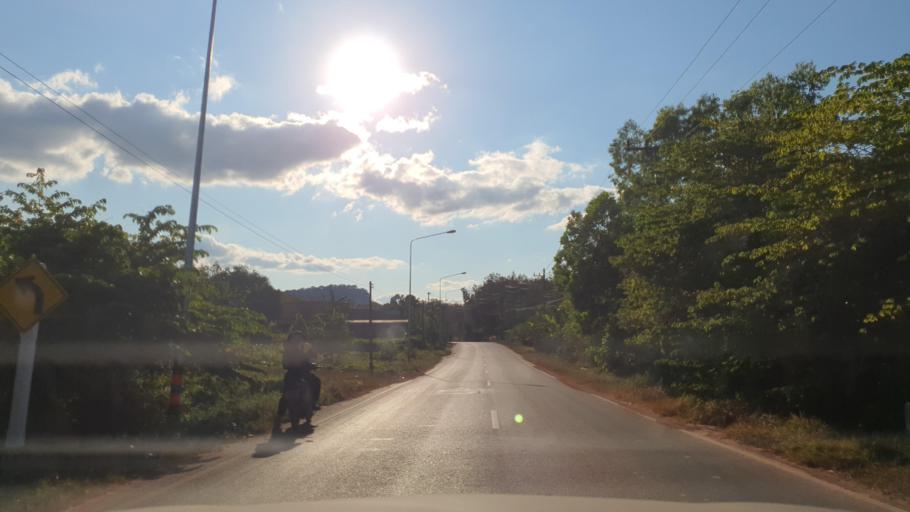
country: TH
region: Changwat Bueng Kan
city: Si Wilai
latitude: 18.1497
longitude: 103.9006
